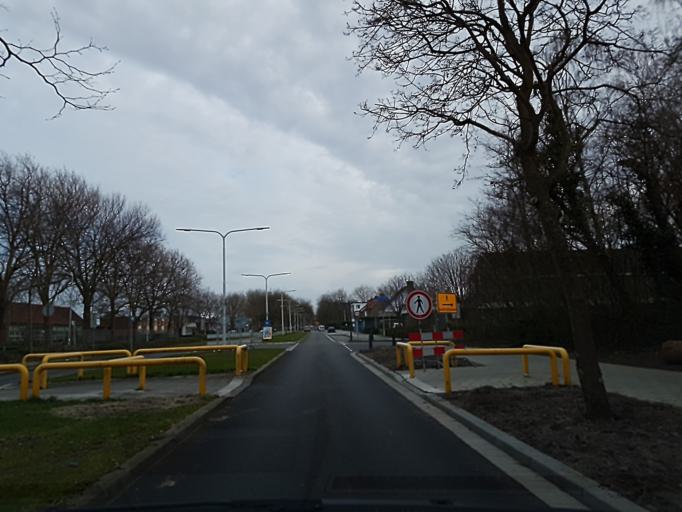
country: NL
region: Zeeland
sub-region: Gemeente Terneuzen
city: Terneuzen
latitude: 51.3302
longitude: 3.8375
